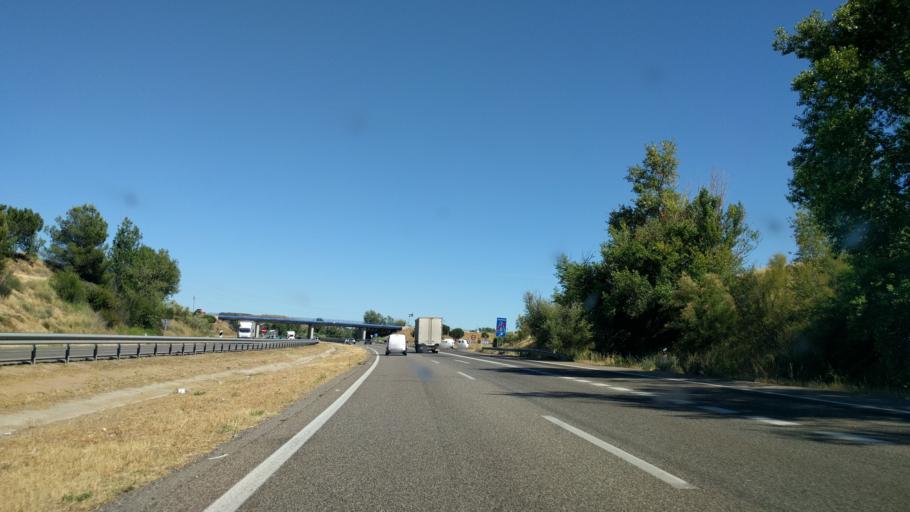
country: ES
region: Catalonia
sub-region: Provincia de Lleida
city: Alcoletge
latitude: 41.6583
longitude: 0.6553
